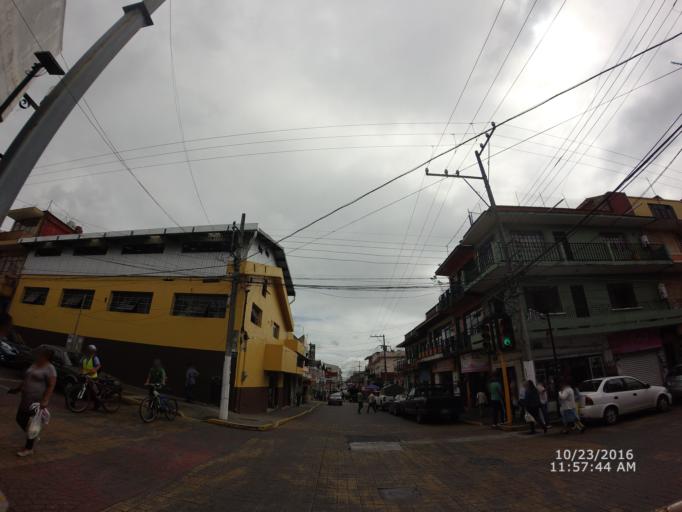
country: MX
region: Veracruz
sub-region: Xalapa
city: Xalapa de Enriquez
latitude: 19.5329
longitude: -96.9225
